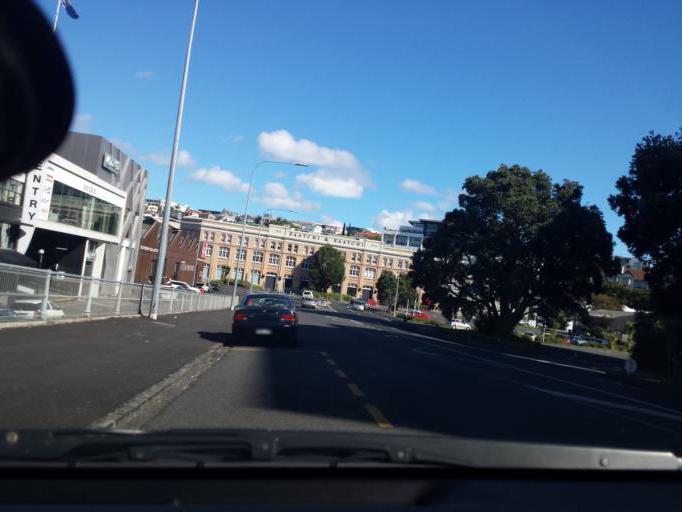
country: NZ
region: Auckland
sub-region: Auckland
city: Auckland
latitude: -36.8491
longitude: 174.7829
